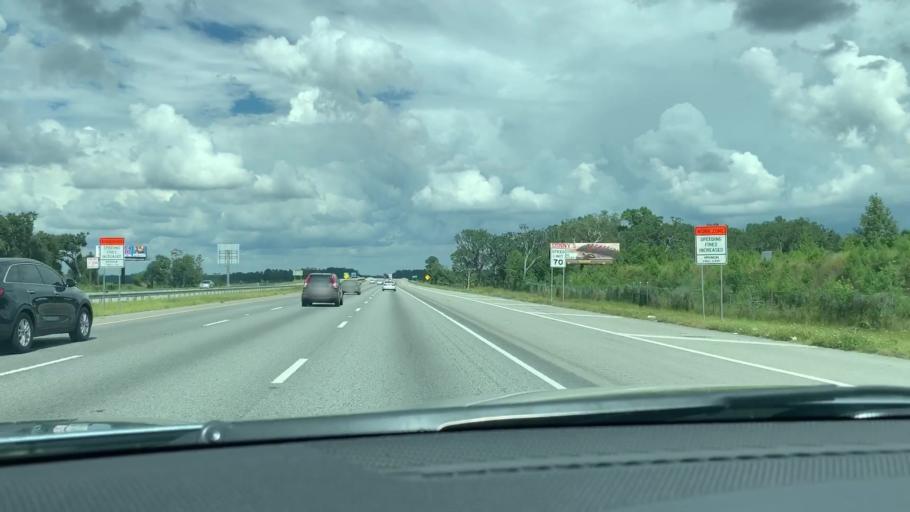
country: US
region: Georgia
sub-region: Glynn County
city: Dock Junction
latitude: 31.1473
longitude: -81.5683
